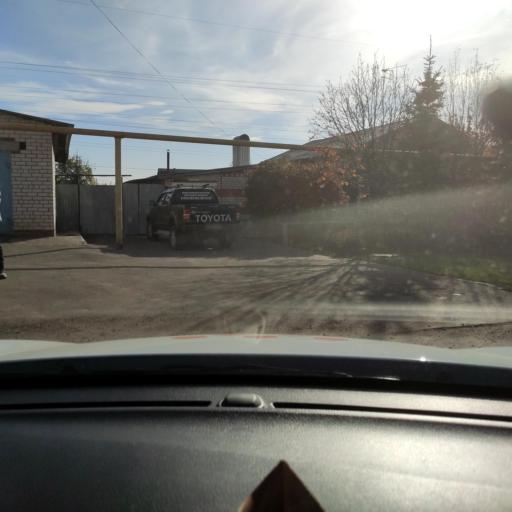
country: RU
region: Tatarstan
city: Vysokaya Gora
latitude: 55.8046
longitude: 49.2695
